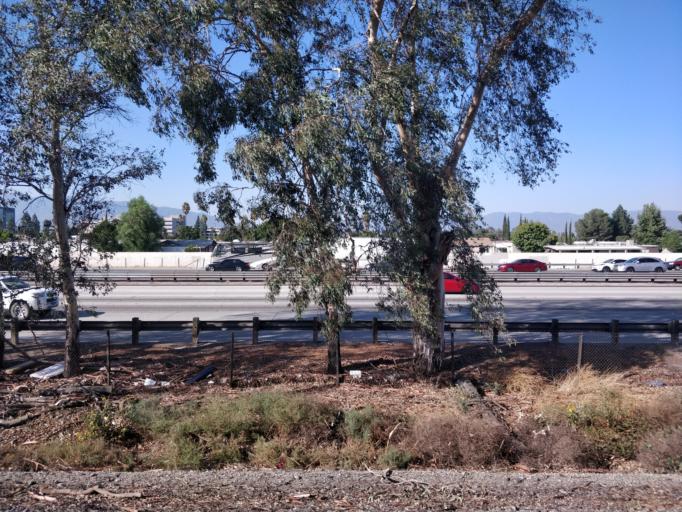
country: US
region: California
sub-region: San Bernardino County
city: Fontana
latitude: 34.0666
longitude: -117.4274
